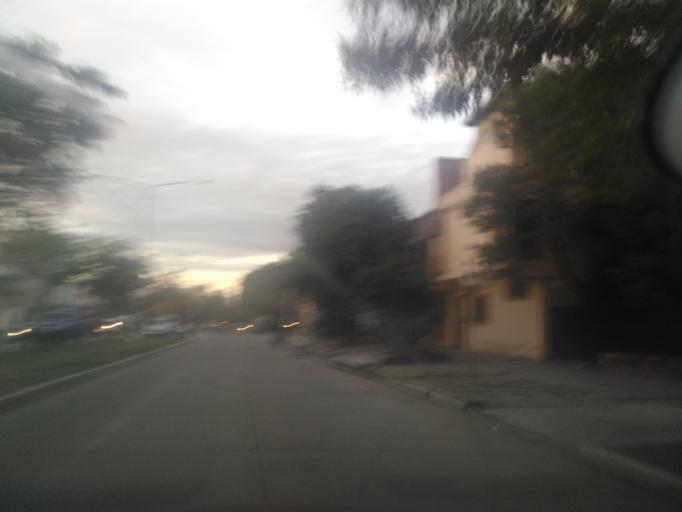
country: AR
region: Chaco
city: Resistencia
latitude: -27.4650
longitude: -58.9932
